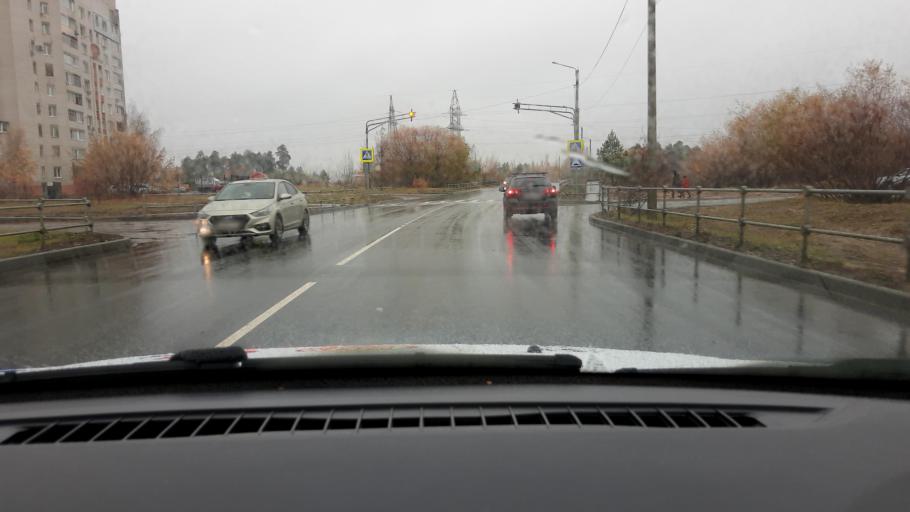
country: RU
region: Nizjnij Novgorod
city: Dzerzhinsk
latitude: 56.2344
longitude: 43.4085
